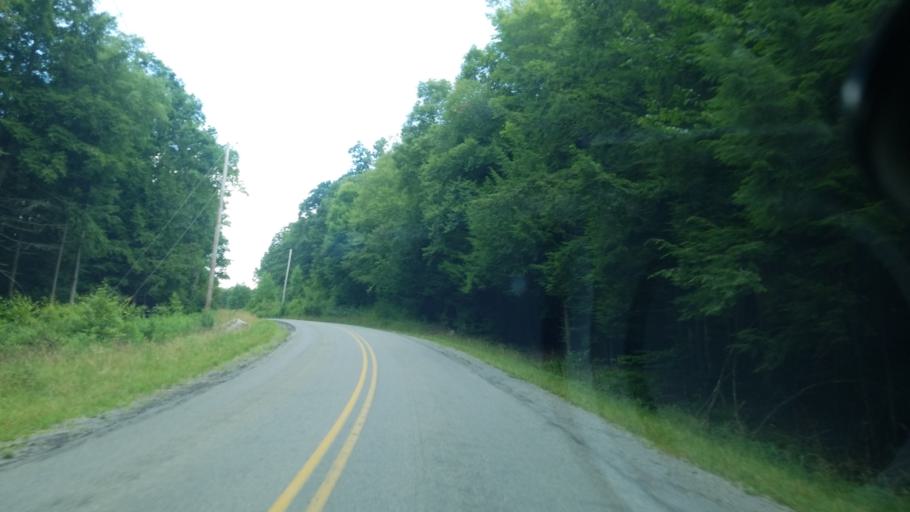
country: US
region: Pennsylvania
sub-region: Jefferson County
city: Brookville
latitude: 41.2300
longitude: -79.0480
